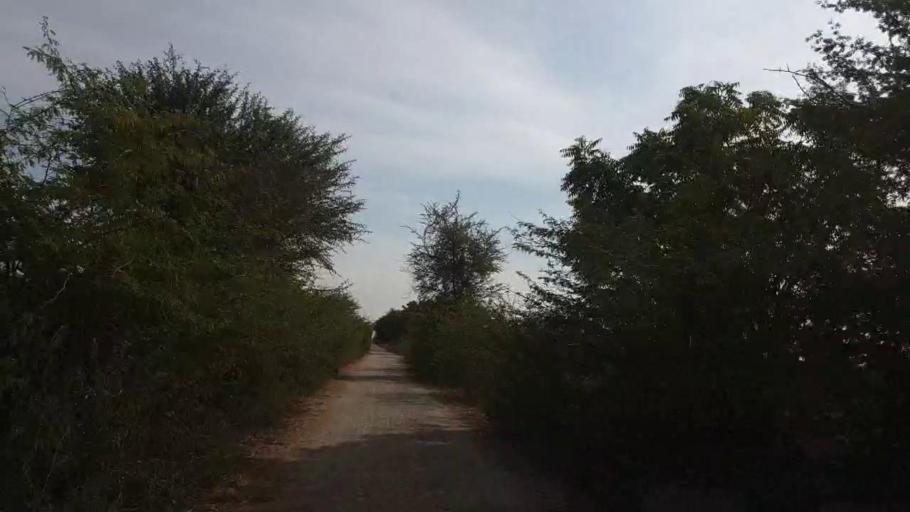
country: PK
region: Sindh
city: Nabisar
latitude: 25.0229
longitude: 69.5623
